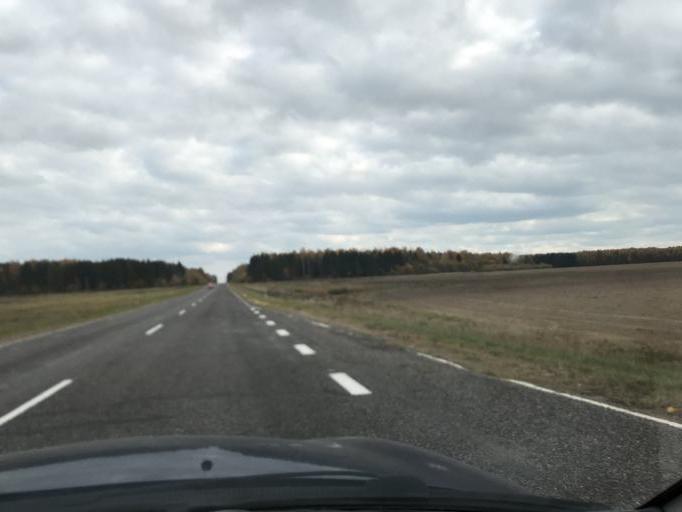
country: BY
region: Grodnenskaya
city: Lida
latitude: 53.7440
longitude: 25.3258
